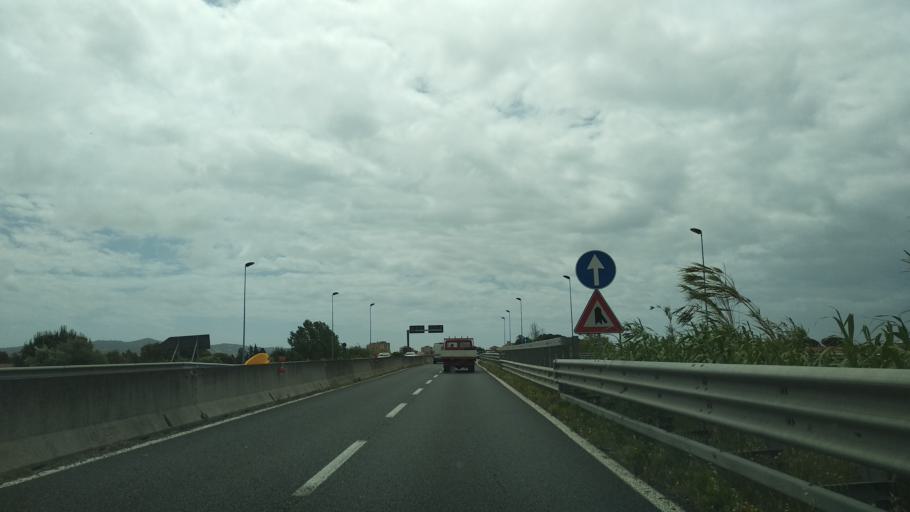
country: IT
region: Tuscany
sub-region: Provincia di Livorno
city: Livorno
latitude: 43.5484
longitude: 10.3421
